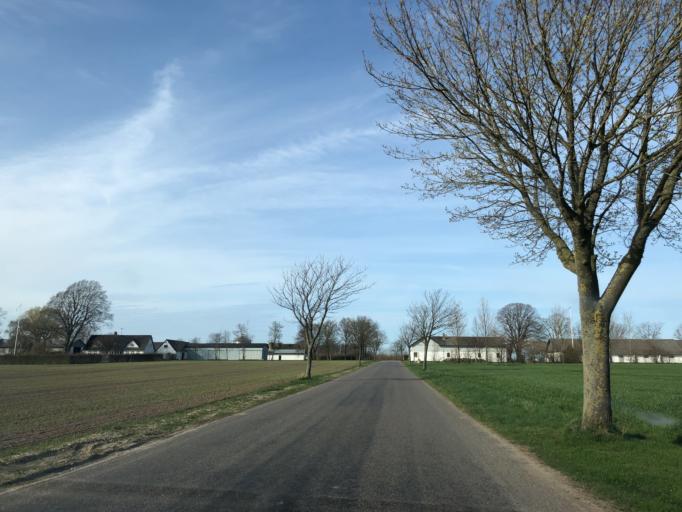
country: DK
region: Zealand
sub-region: Stevns Kommune
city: Store Heddinge
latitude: 55.2895
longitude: 12.4448
